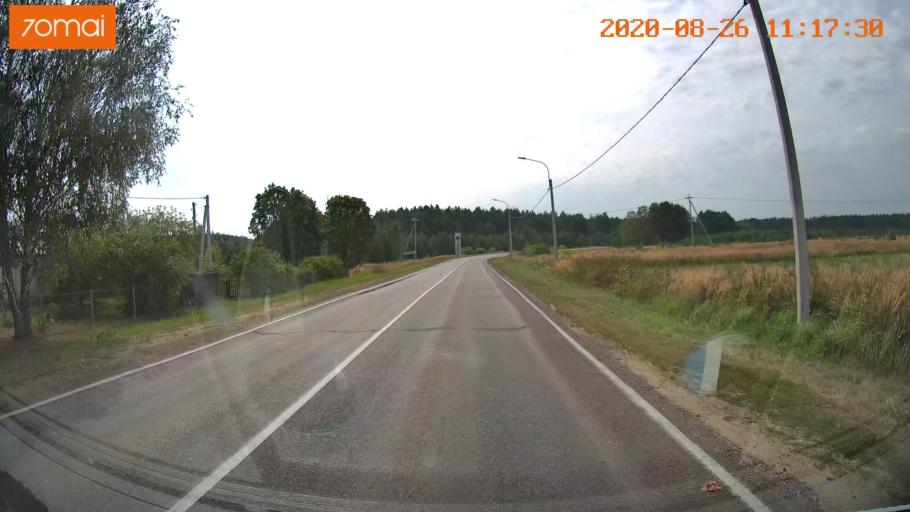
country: RU
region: Rjazan
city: Shilovo
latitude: 54.4183
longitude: 41.1099
